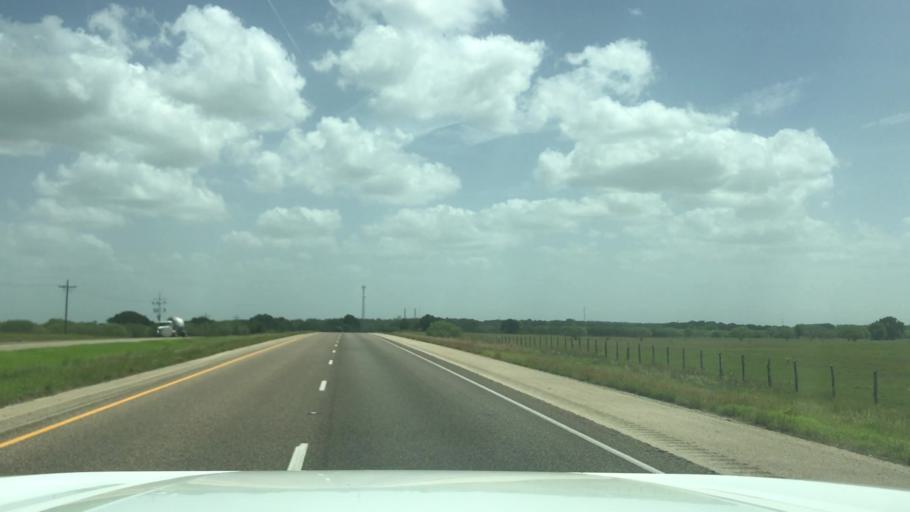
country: US
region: Texas
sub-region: Robertson County
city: Calvert
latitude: 31.1287
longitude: -96.7164
